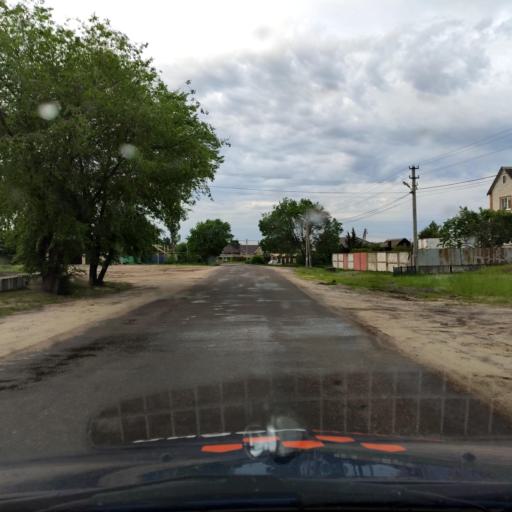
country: RU
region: Voronezj
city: Pridonskoy
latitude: 51.6735
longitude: 39.0770
